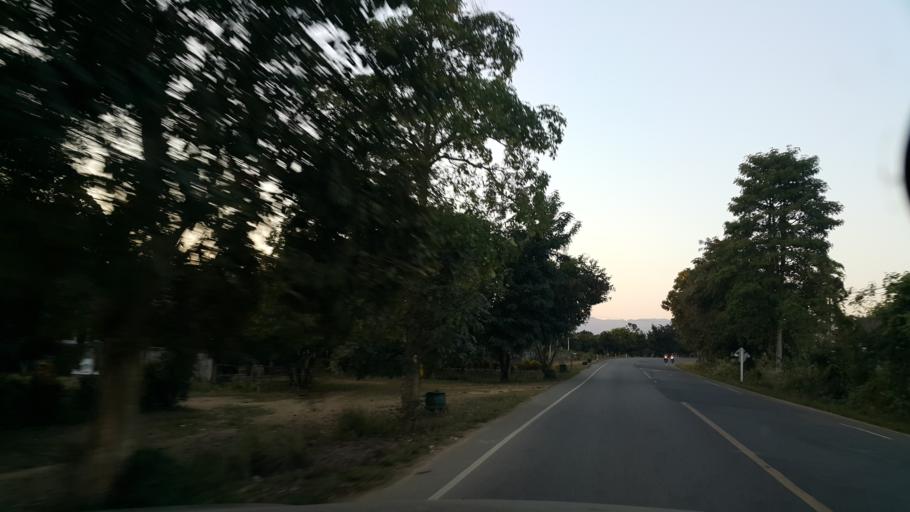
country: TH
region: Phrae
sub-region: Amphoe Wang Chin
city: Wang Chin
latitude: 17.8463
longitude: 99.6290
